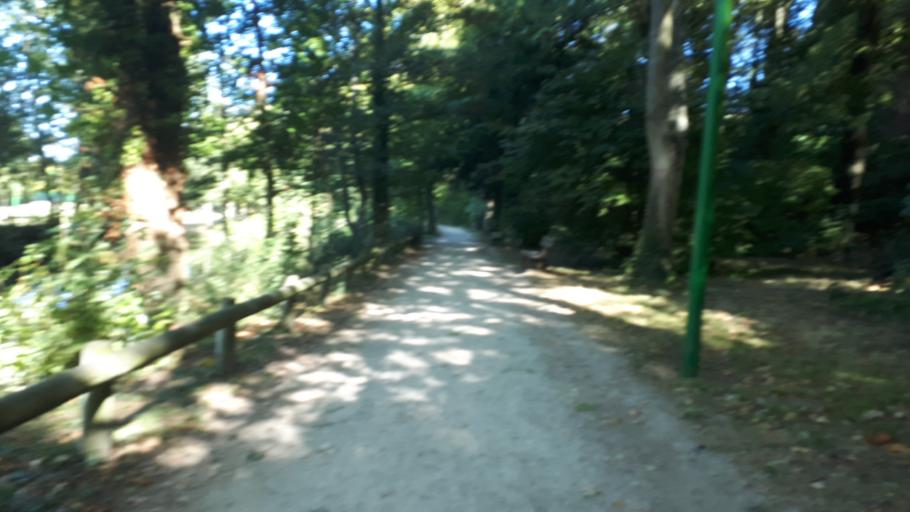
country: FR
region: Centre
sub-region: Departement d'Eure-et-Loir
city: Chartres
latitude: 48.4376
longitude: 1.5005
